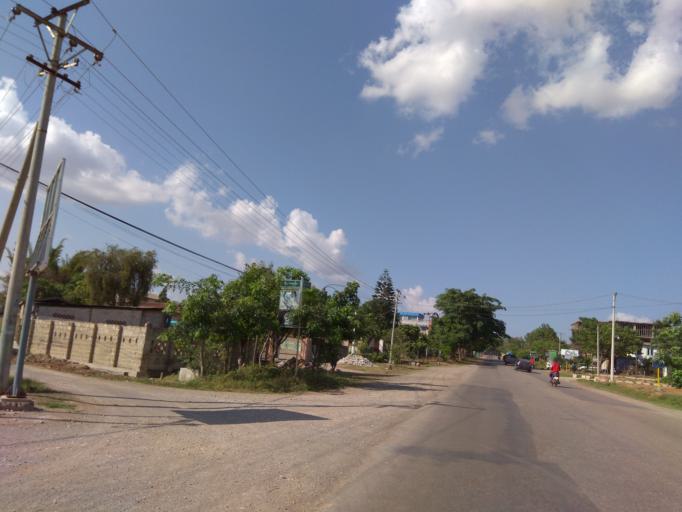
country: MM
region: Shan
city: Taunggyi
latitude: 20.6604
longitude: 96.6438
